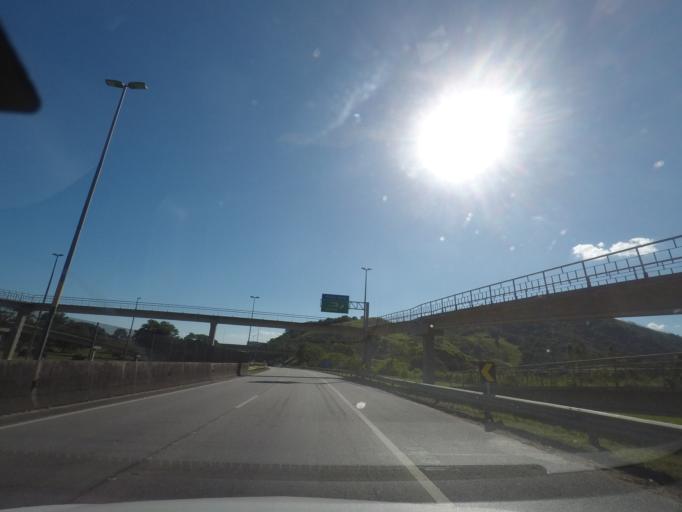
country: BR
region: Rio de Janeiro
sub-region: Guapimirim
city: Guapimirim
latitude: -22.6549
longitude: -43.0868
